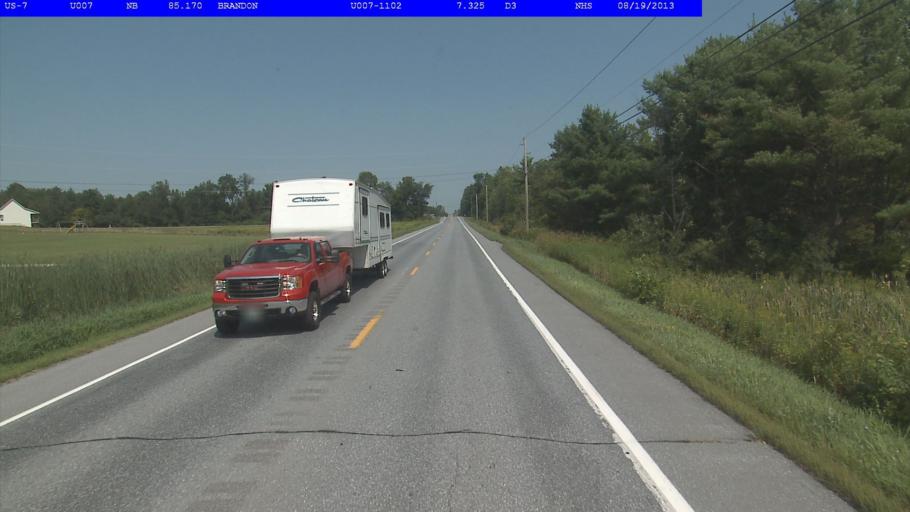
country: US
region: Vermont
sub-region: Rutland County
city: Brandon
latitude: 43.8418
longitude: -73.1061
